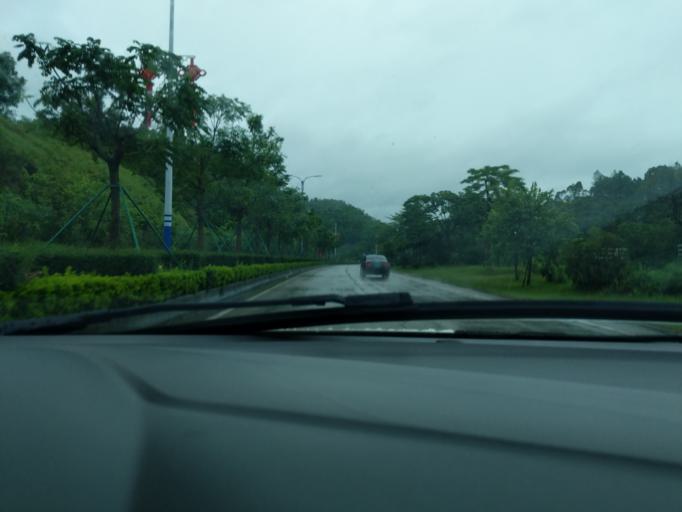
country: CN
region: Guangdong
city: Pingshi
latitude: 22.2272
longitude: 112.3132
